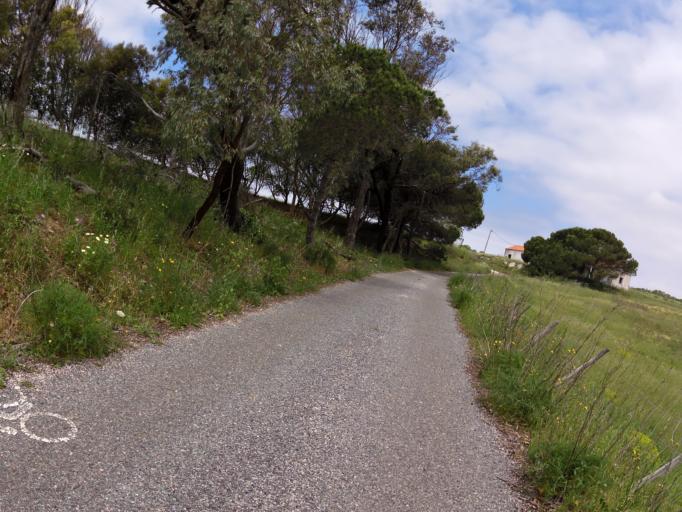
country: PT
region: Faro
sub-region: Vila do Bispo
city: Vila do Bispo
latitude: 37.0782
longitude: -8.8784
